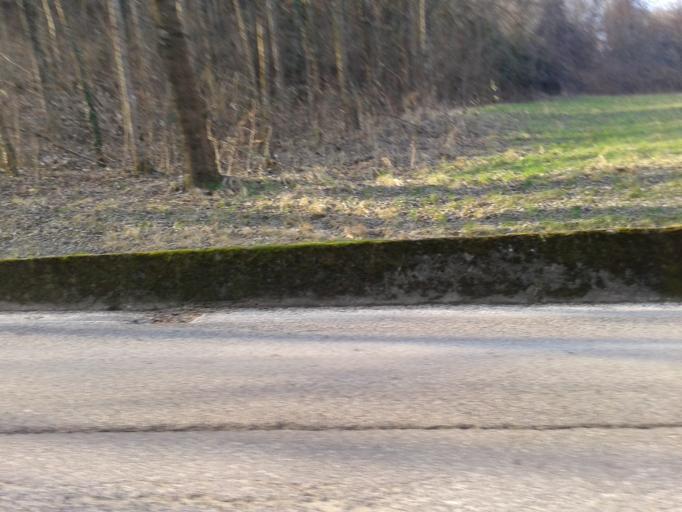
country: IT
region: Veneto
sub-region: Provincia di Vicenza
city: Monte di Malo
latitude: 45.6697
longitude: 11.3678
